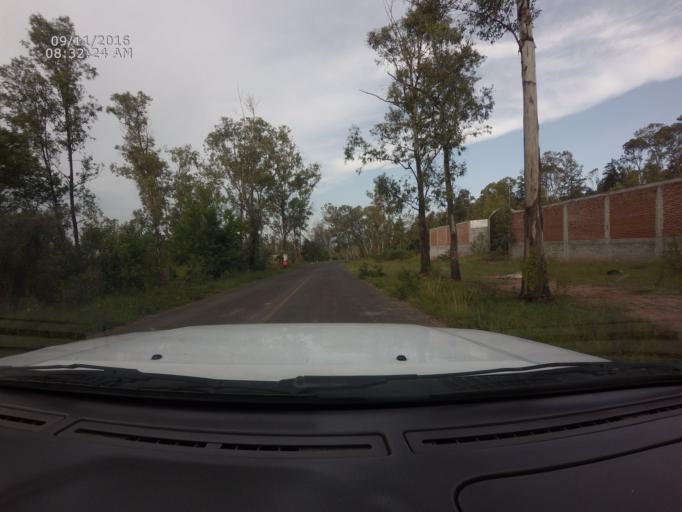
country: MX
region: Michoacan
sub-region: Morelia
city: Morelos
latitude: 19.6293
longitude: -101.2487
